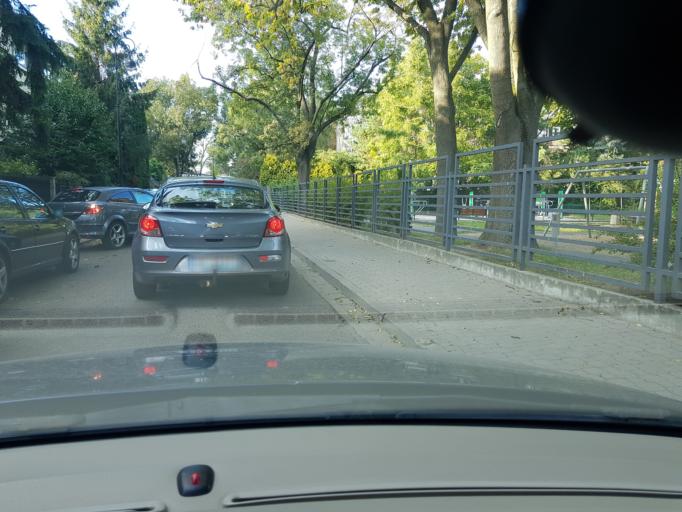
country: PL
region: Masovian Voivodeship
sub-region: Warszawa
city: Praga Poludnie
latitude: 52.2346
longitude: 21.0582
